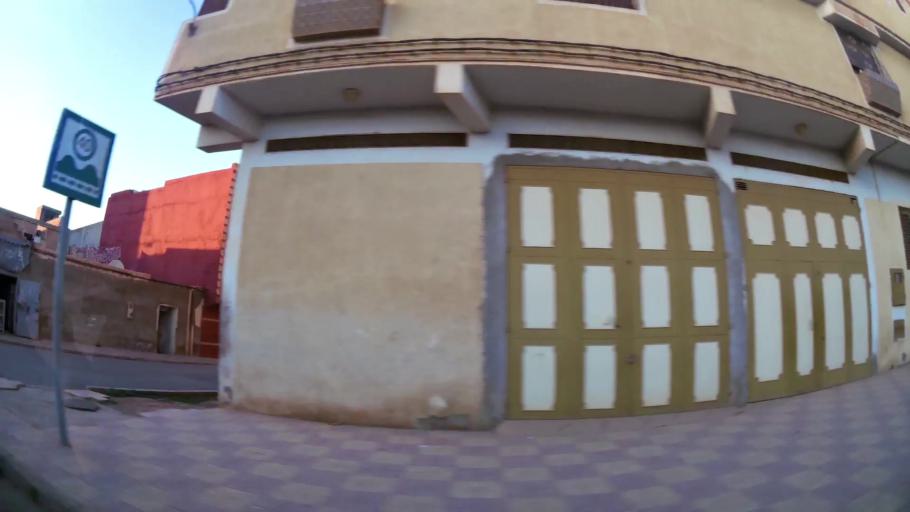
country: MA
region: Oriental
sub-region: Berkane-Taourirt
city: Berkane
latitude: 34.9180
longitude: -2.3151
